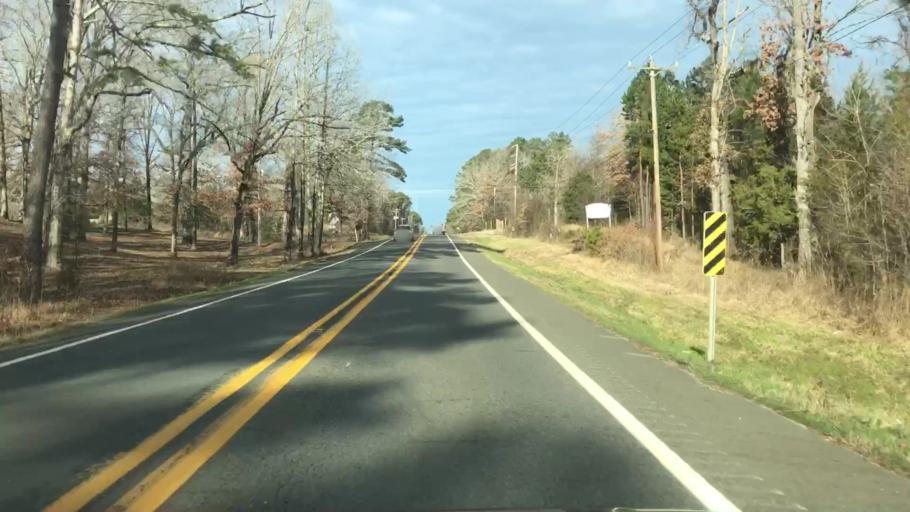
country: US
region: Arkansas
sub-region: Montgomery County
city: Mount Ida
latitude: 34.5399
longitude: -93.6049
